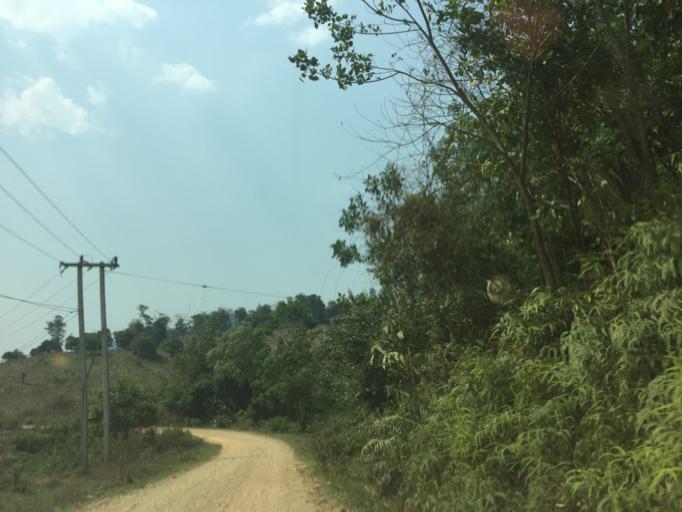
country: TH
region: Nan
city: Song Khwae
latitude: 19.7370
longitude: 100.7217
